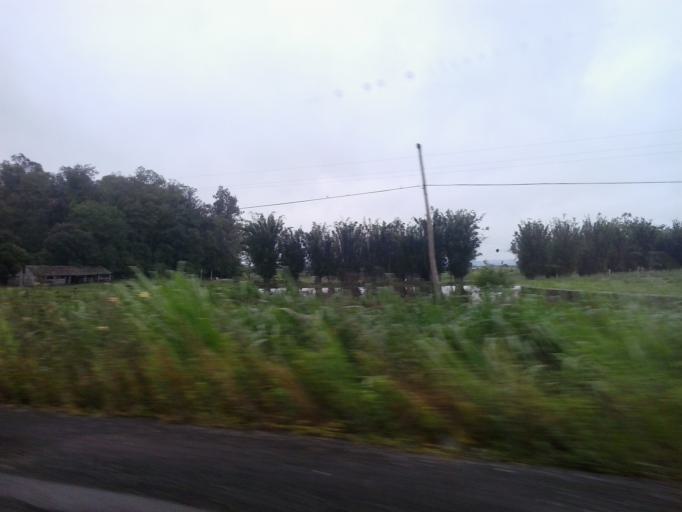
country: BR
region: Rio Grande do Sul
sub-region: Candelaria
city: Candelaria
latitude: -29.7300
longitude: -53.1948
